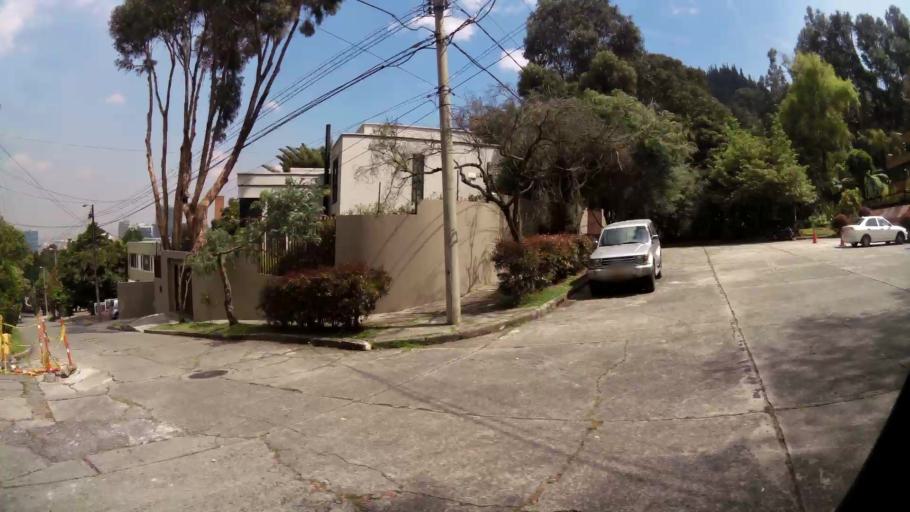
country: CO
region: Bogota D.C.
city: Barrio San Luis
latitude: 4.6871
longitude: -74.0265
